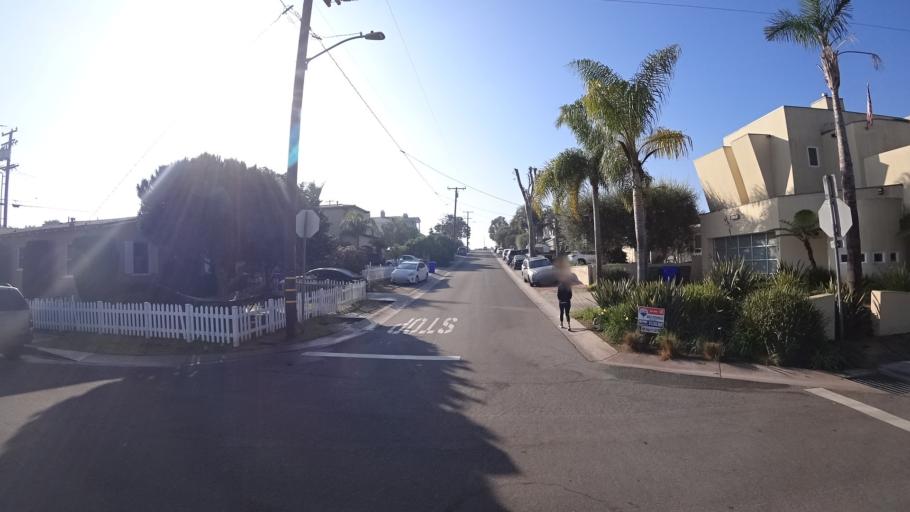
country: US
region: California
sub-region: Los Angeles County
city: Manhattan Beach
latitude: 33.8890
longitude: -118.3969
